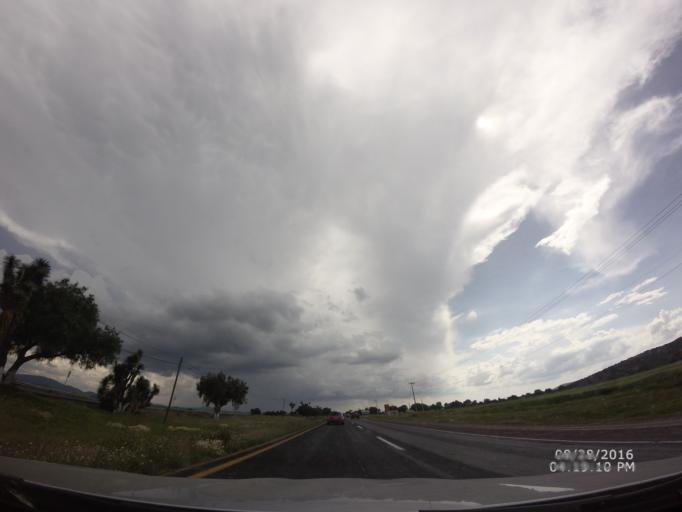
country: MX
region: Hidalgo
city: Zapotlan de Juarez
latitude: 19.9570
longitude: -98.8657
